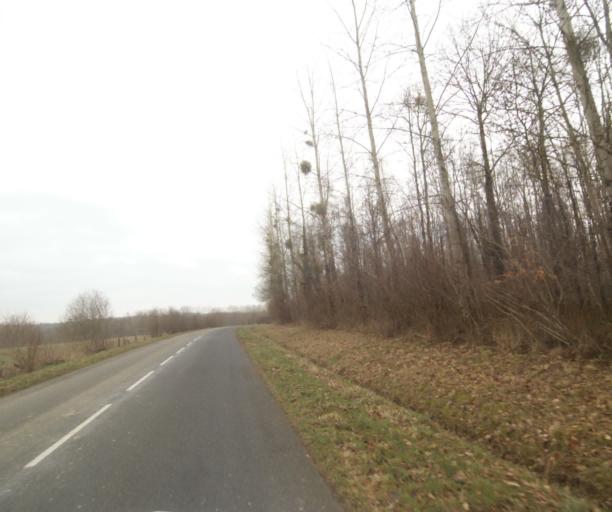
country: FR
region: Champagne-Ardenne
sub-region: Departement de la Marne
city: Pargny-sur-Saulx
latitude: 48.7404
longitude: 4.8675
